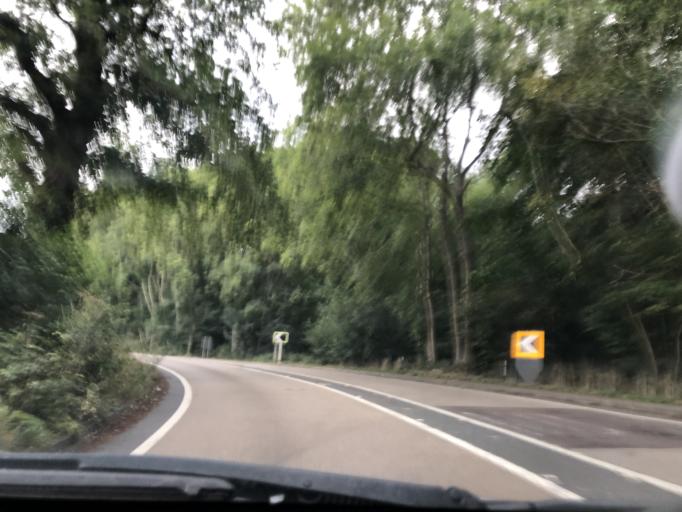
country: GB
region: England
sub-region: Kent
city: Sevenoaks
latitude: 51.2481
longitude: 0.2069
